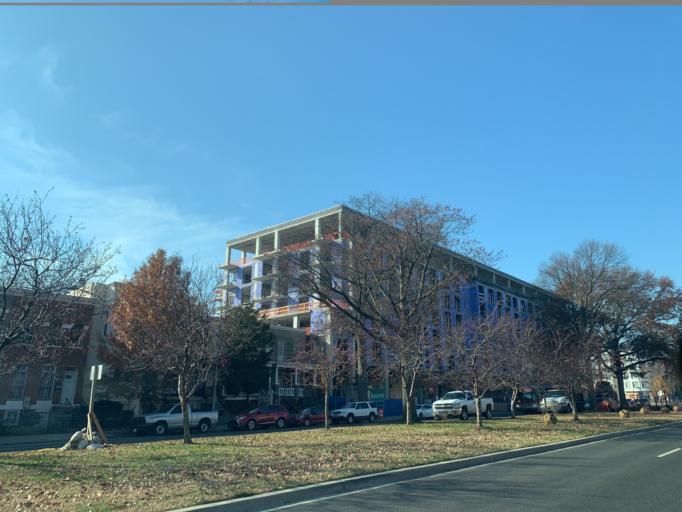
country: US
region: Maryland
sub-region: Prince George's County
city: Hillcrest Heights
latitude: 38.8797
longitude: -76.9838
